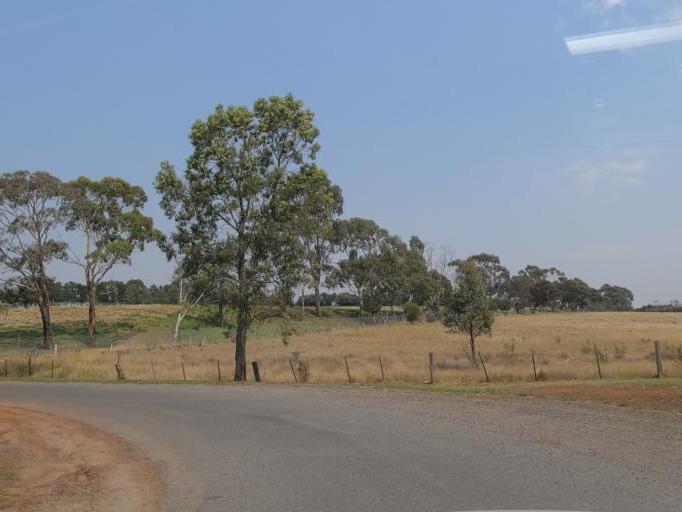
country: AU
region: Victoria
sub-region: Hume
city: Greenvale
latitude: -37.6382
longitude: 144.8298
